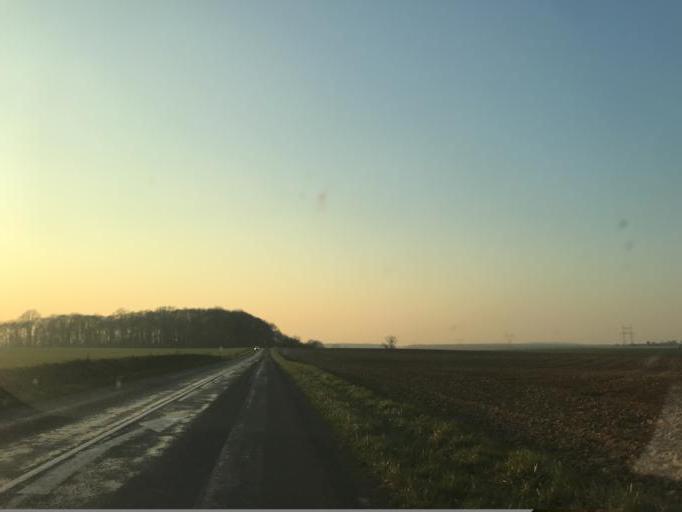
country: FR
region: Ile-de-France
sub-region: Departement de Seine-et-Marne
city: Charny
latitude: 49.0087
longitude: 2.7623
